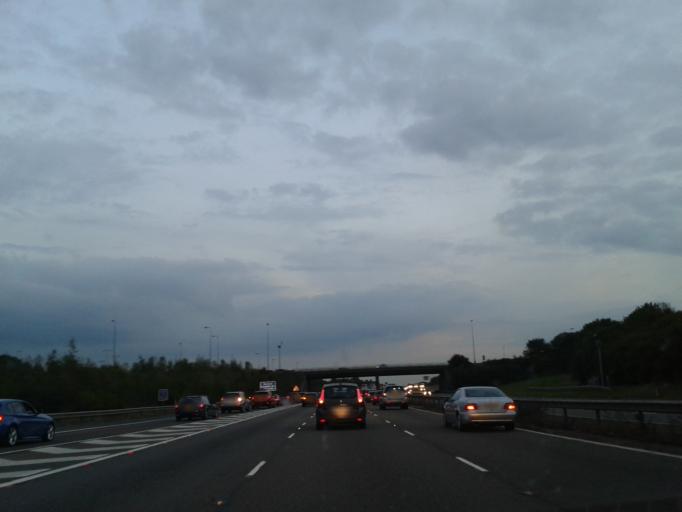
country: GB
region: England
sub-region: Oxfordshire
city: Somerton
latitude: 51.9501
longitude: -1.2062
